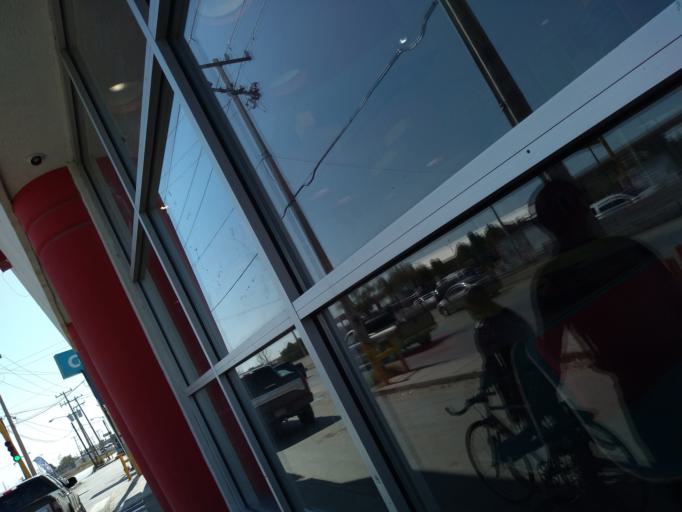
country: US
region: Texas
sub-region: El Paso County
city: El Paso
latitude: 31.7528
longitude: -106.4987
